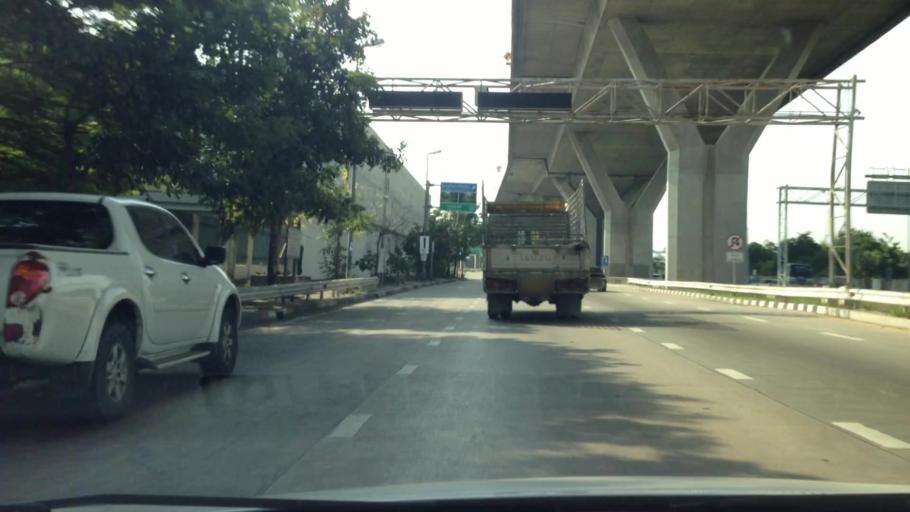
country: TH
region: Samut Prakan
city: Phra Pradaeng
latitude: 13.6519
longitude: 100.5413
